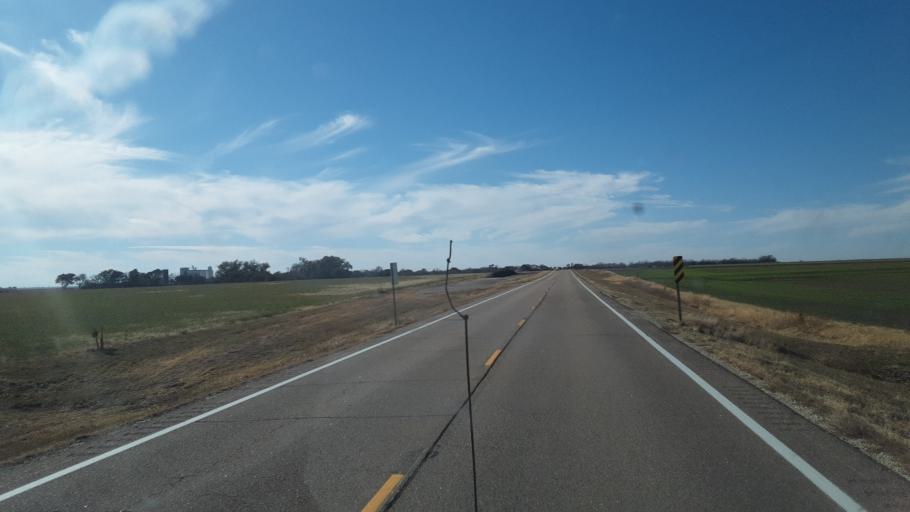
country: US
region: Kansas
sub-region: Pawnee County
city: Larned
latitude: 38.1894
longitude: -99.2893
